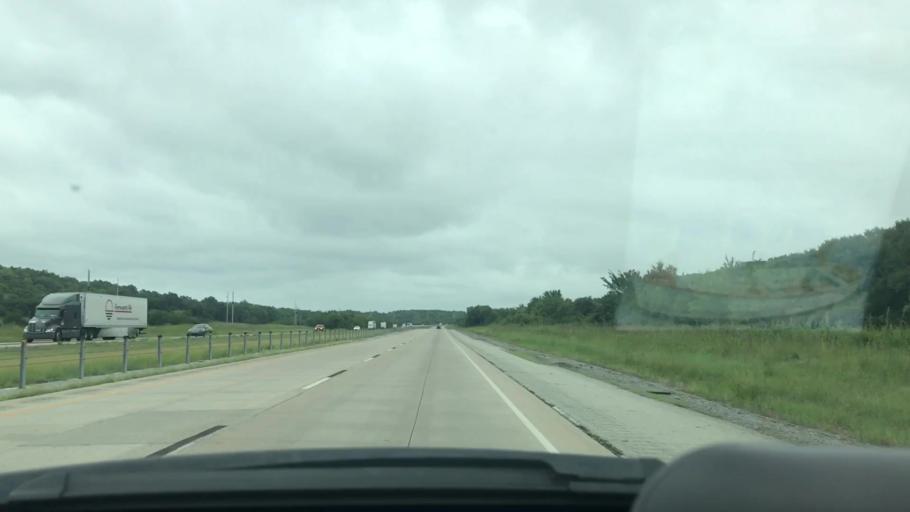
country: US
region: Oklahoma
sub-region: Coal County
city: Coalgate
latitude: 34.5538
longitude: -96.0205
